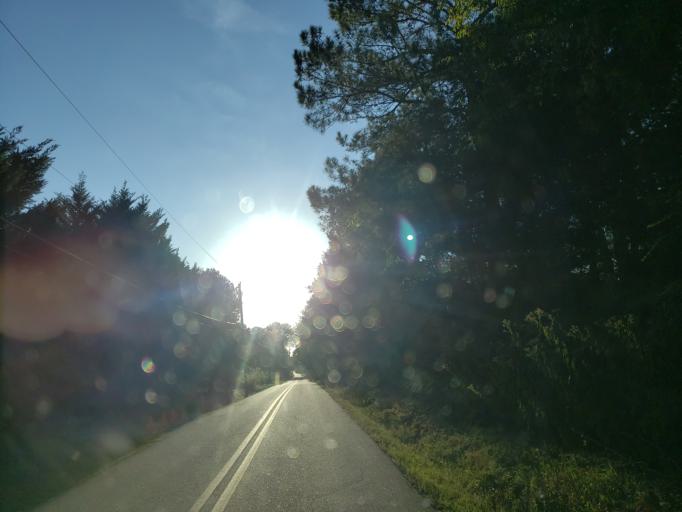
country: US
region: Georgia
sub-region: Bartow County
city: Euharlee
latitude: 34.2328
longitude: -84.9552
